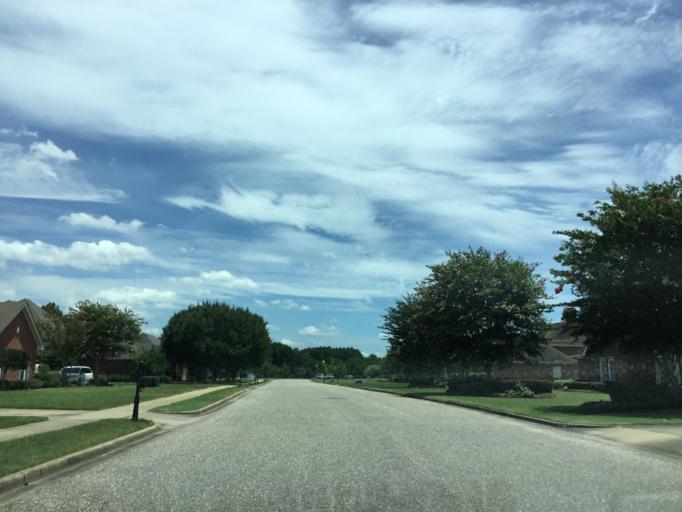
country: US
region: Alabama
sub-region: Montgomery County
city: Pike Road
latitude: 32.3788
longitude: -86.1328
